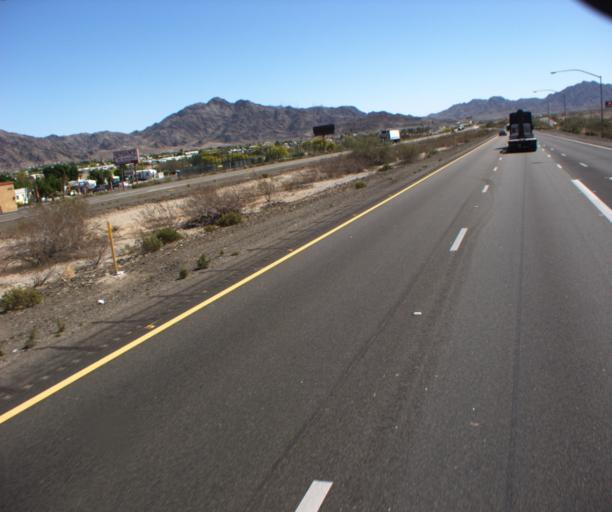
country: US
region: Arizona
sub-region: Yuma County
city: Fortuna Foothills
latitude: 32.6688
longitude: -114.4041
